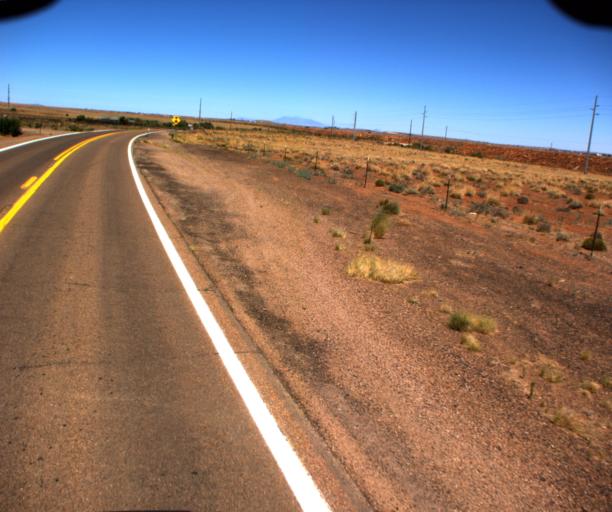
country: US
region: Arizona
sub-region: Navajo County
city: Winslow
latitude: 35.0057
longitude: -110.7001
